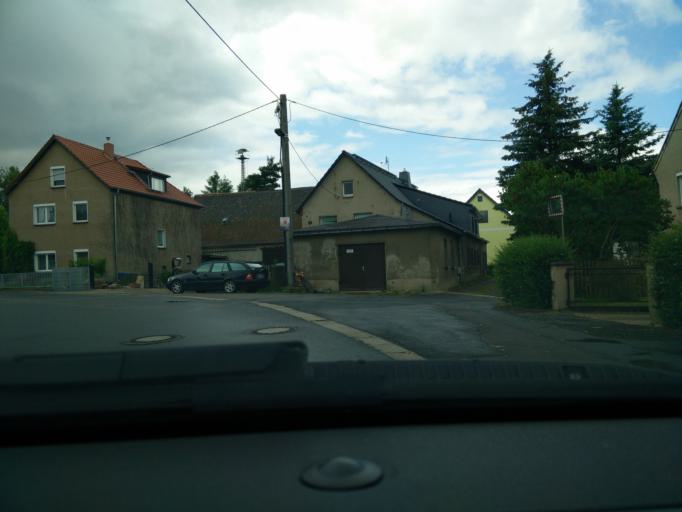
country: DE
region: Saxony
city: Grossbothen
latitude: 51.1875
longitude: 12.7415
